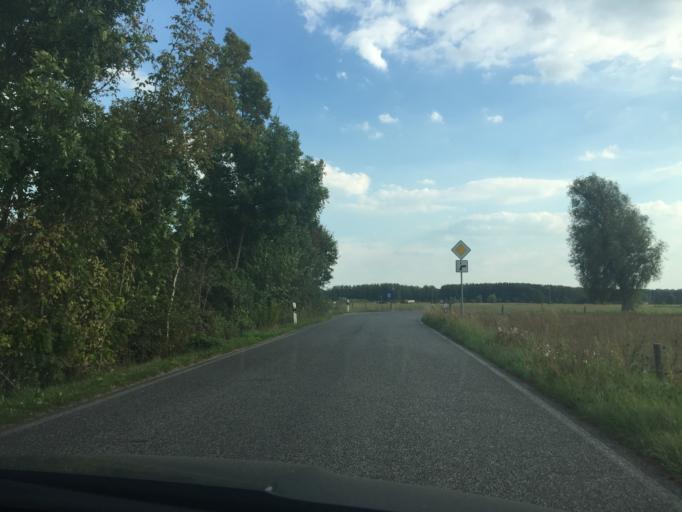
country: DE
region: Brandenburg
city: Spreenhagen
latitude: 52.3541
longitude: 13.8435
